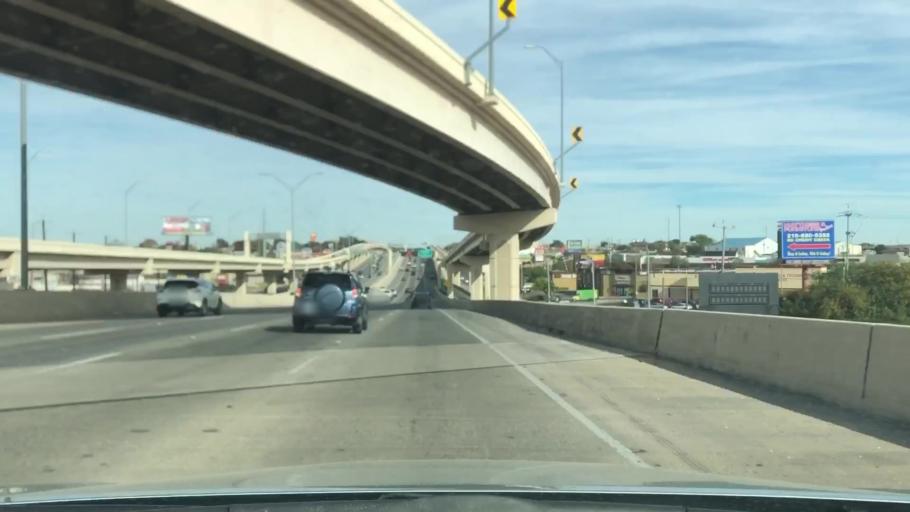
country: US
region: Texas
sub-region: Bexar County
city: Leon Valley
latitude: 29.4828
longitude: -98.5996
